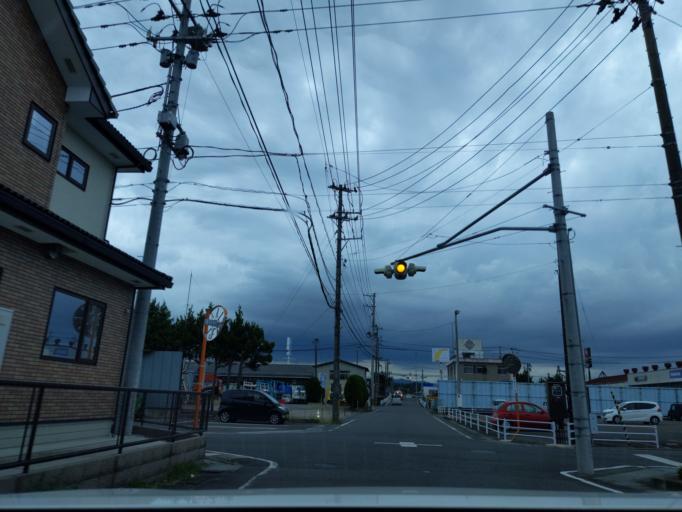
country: JP
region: Fukushima
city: Koriyama
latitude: 37.3563
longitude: 140.3653
